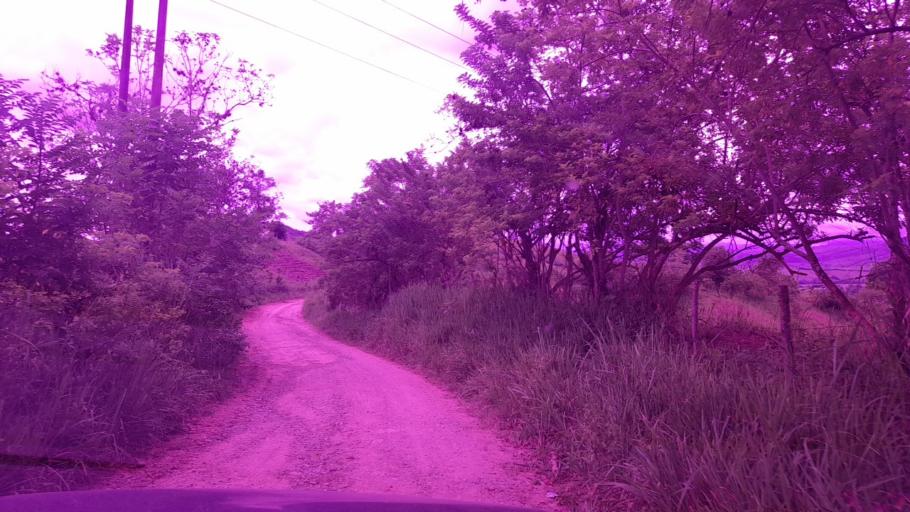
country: CO
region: Valle del Cauca
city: Andalucia
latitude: 4.1726
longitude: -76.0982
